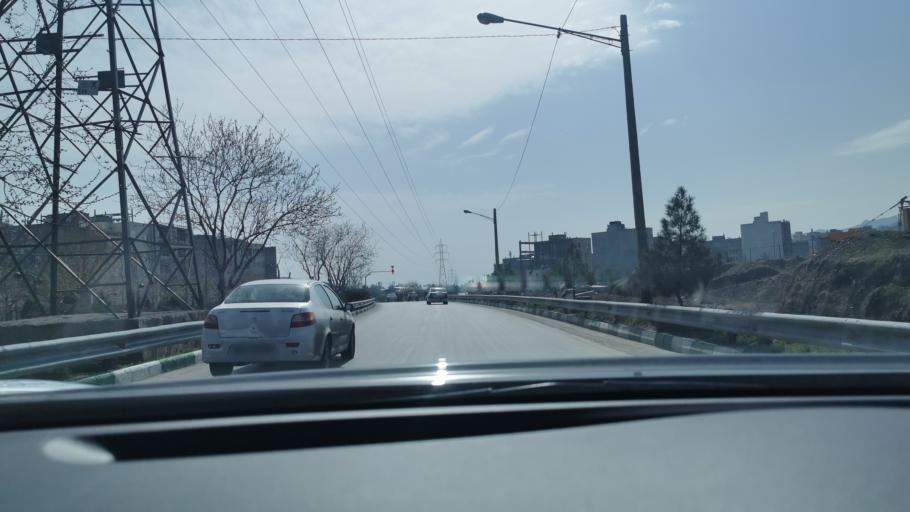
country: IR
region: Razavi Khorasan
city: Mashhad
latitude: 36.2841
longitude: 59.5419
